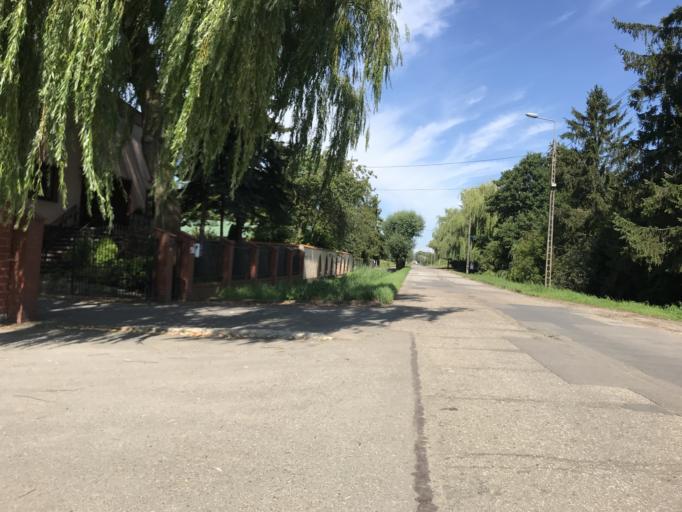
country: PL
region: Pomeranian Voivodeship
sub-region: Gdansk
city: Gdansk
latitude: 54.3300
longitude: 18.6832
